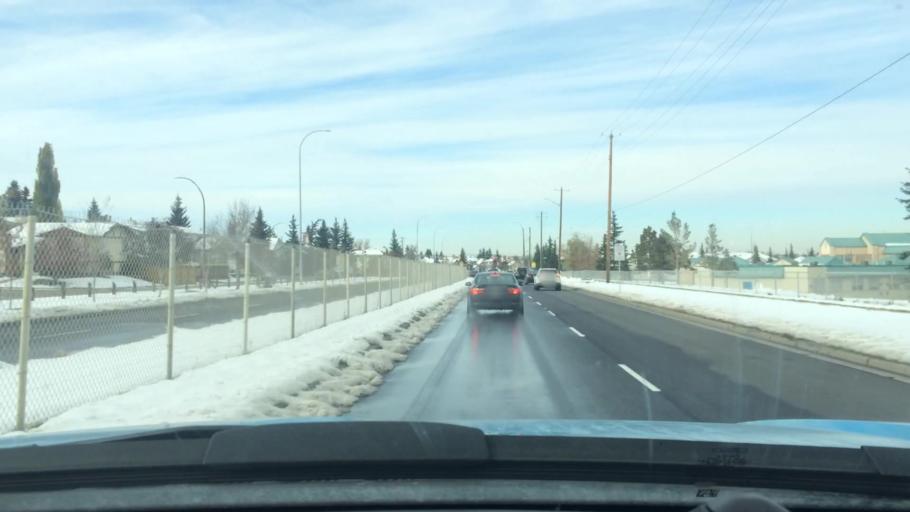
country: CA
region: Alberta
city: Calgary
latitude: 51.1381
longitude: -114.1081
